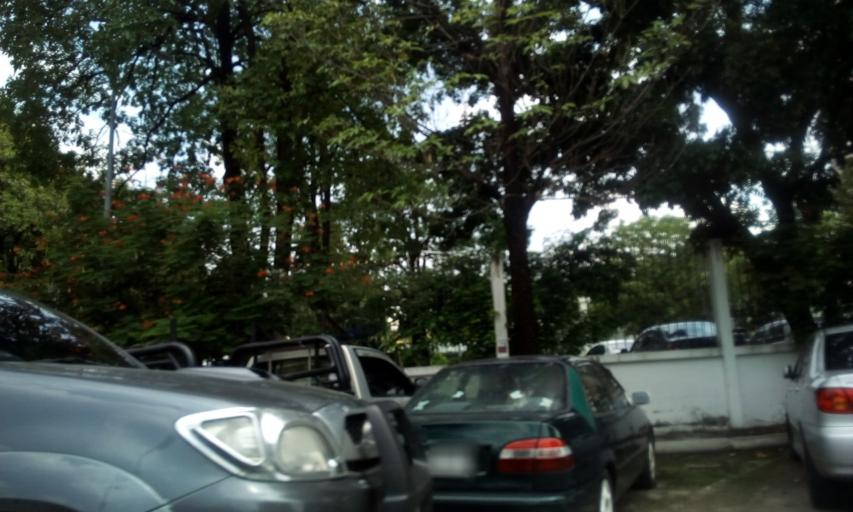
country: TH
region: Bangkok
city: Lak Si
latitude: 13.9120
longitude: 100.5549
